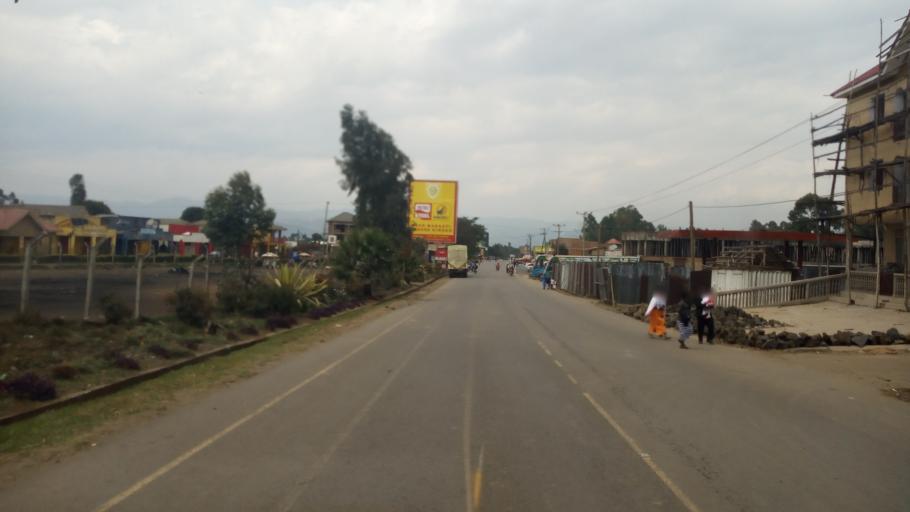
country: UG
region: Western Region
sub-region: Kisoro District
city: Kisoro
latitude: -1.2825
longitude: 29.6945
